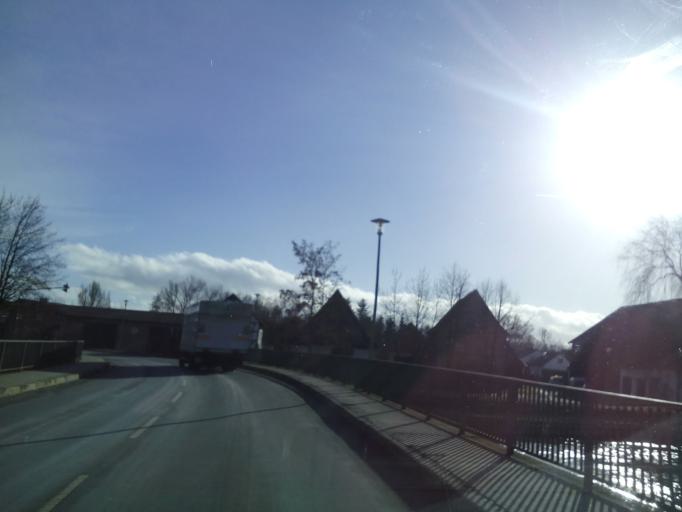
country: DE
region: Bavaria
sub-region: Upper Franconia
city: Marktzeuln
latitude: 50.1661
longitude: 11.1712
